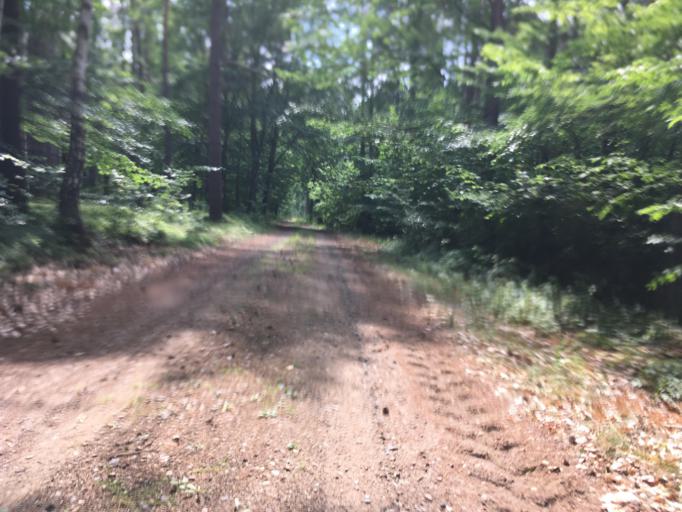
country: DE
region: Brandenburg
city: Joachimsthal
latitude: 53.0011
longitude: 13.7756
